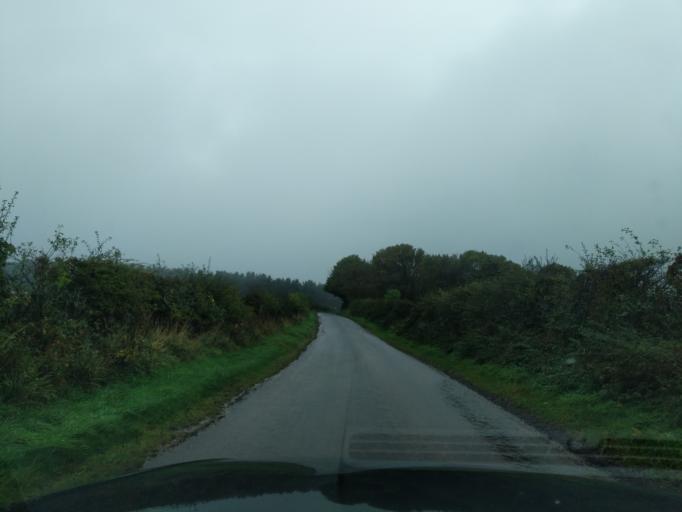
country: GB
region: Scotland
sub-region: East Lothian
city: Dunbar
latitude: 55.9337
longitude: -2.4121
